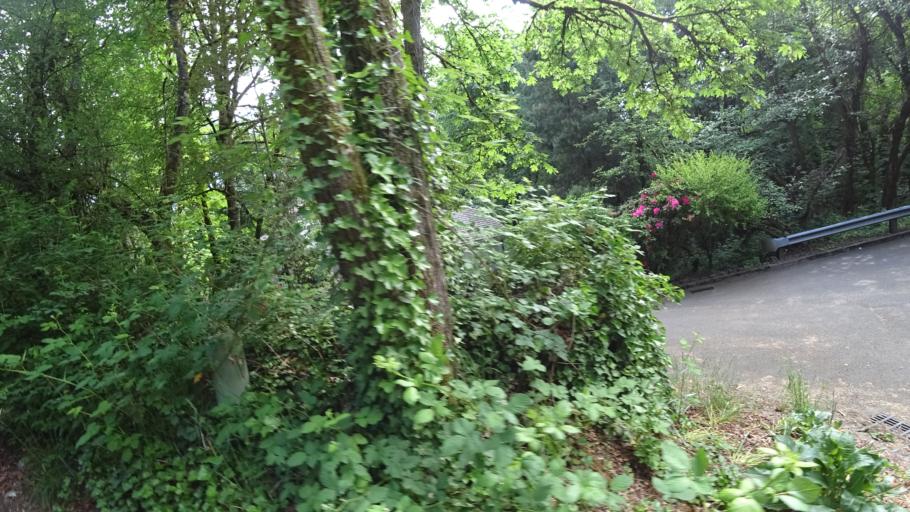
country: US
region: Oregon
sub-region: Multnomah County
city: Portland
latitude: 45.5053
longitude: -122.7112
